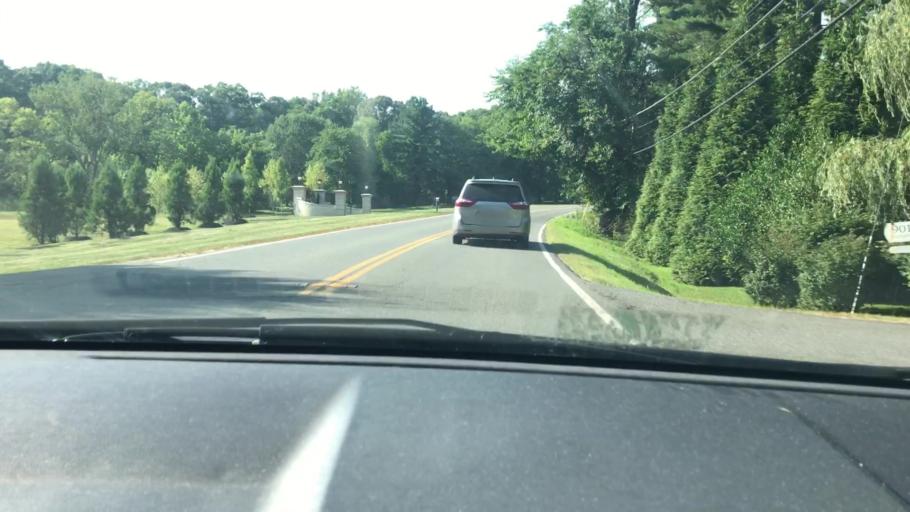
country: US
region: Virginia
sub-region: Fairfax County
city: Great Falls
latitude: 38.9778
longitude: -77.2571
